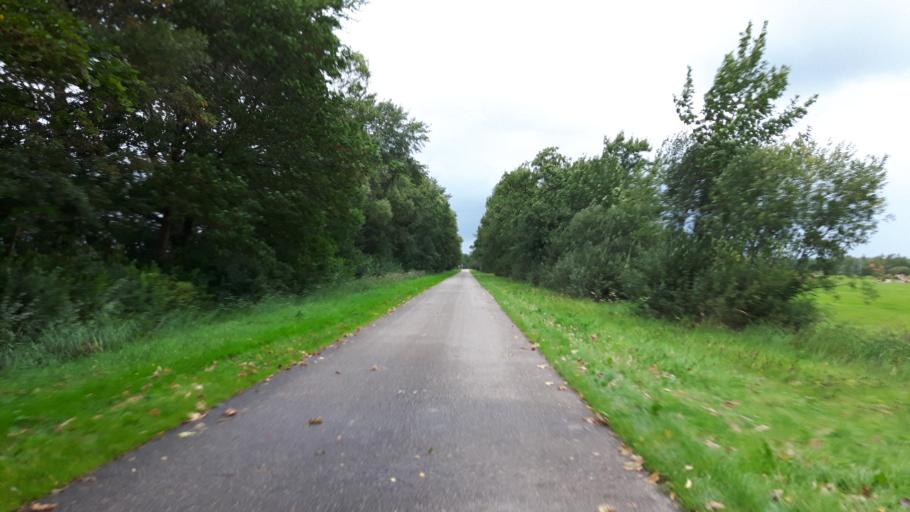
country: NL
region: Friesland
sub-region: Gemeente Dantumadiel
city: Broeksterwald
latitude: 53.2676
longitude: 5.9848
